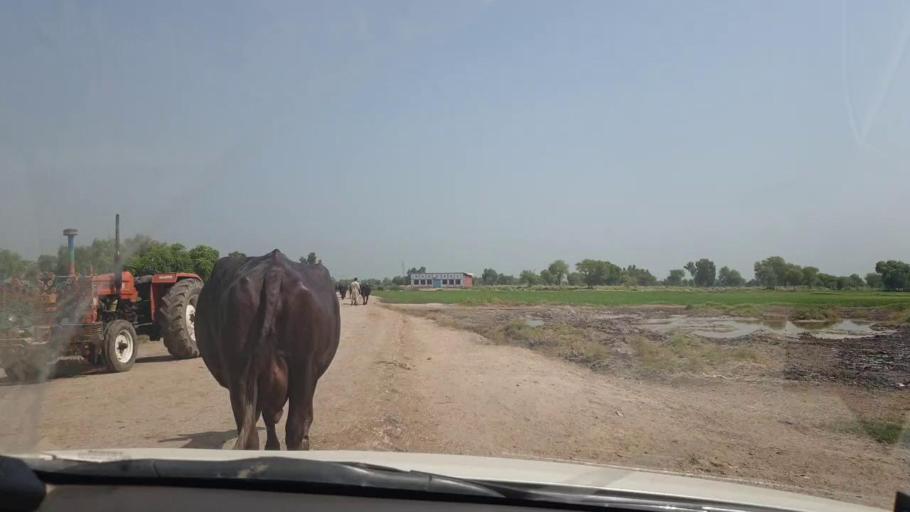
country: PK
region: Sindh
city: Chak
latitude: 27.8795
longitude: 68.7819
